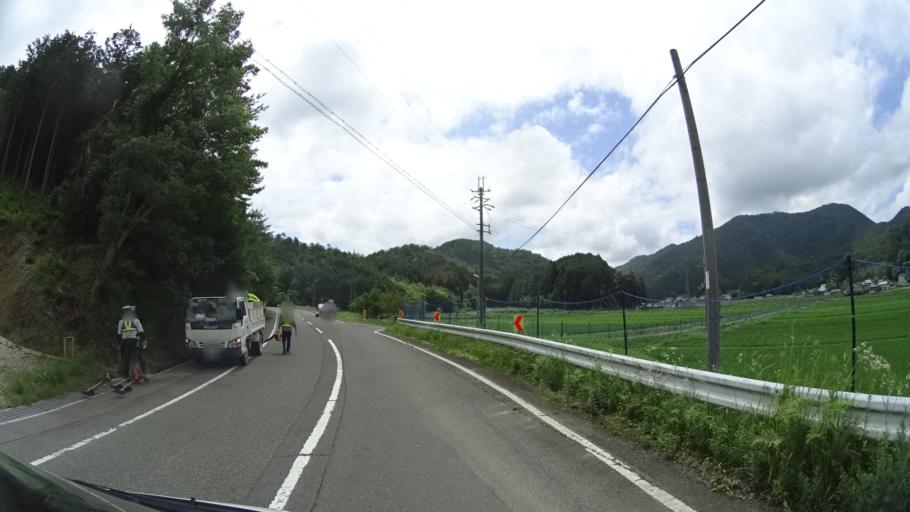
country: JP
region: Kyoto
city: Kameoka
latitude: 35.0831
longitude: 135.4847
